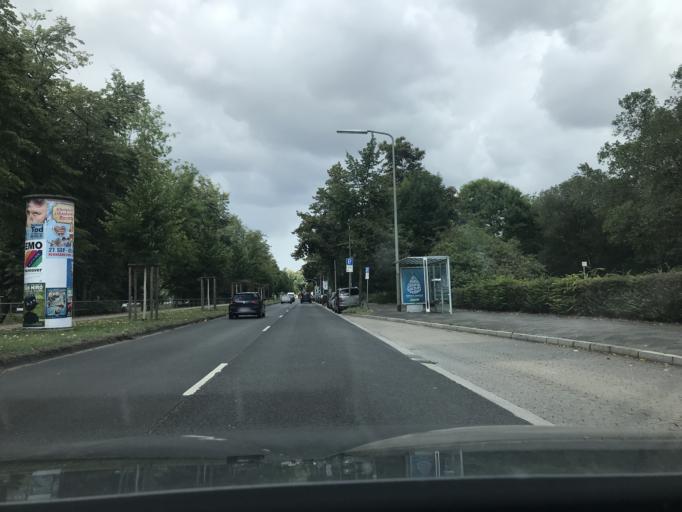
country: DE
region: North Rhine-Westphalia
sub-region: Regierungsbezirk Dusseldorf
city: Dusseldorf
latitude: 51.2434
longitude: 6.8142
